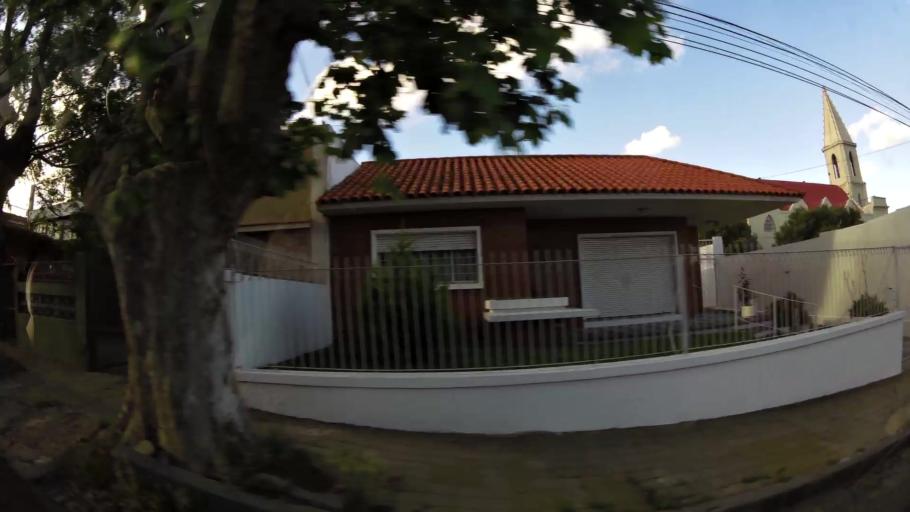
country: UY
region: Montevideo
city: Montevideo
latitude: -34.8880
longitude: -56.2527
